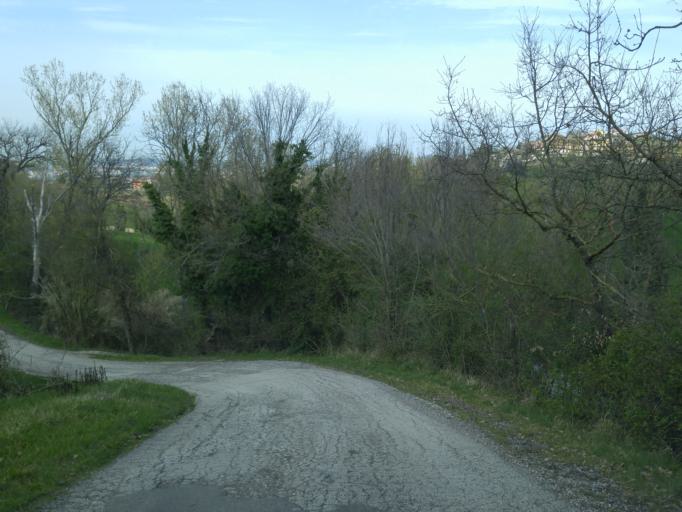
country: IT
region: The Marches
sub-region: Provincia di Pesaro e Urbino
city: Villanova
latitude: 43.7298
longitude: 12.9344
